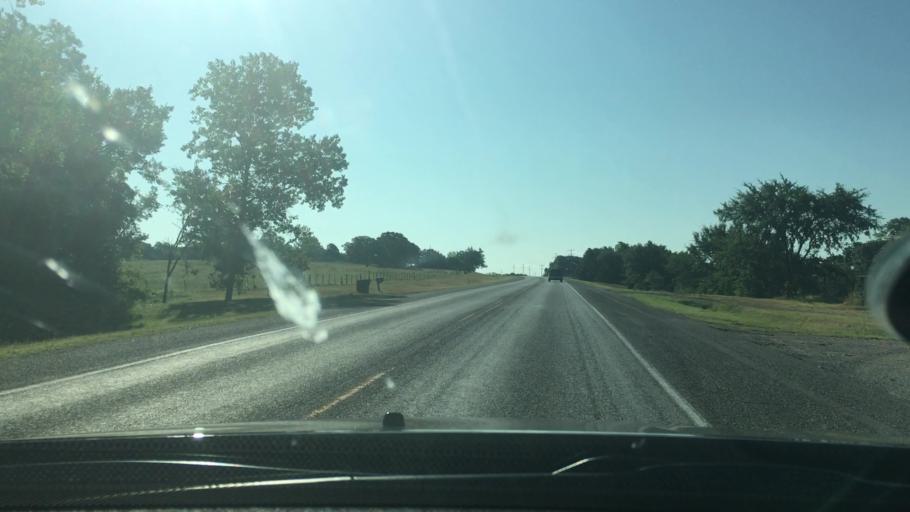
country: US
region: Oklahoma
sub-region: Johnston County
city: Tishomingo
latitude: 34.2389
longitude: -96.7376
